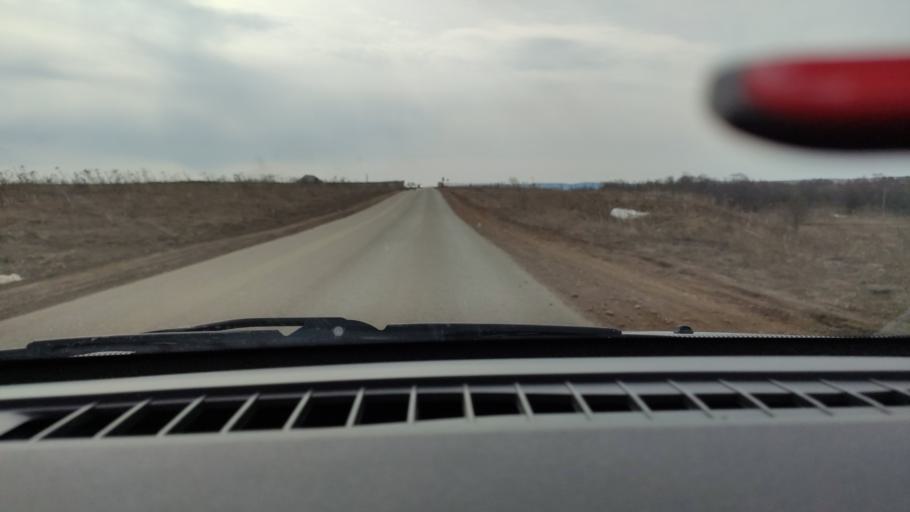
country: RU
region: Perm
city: Kultayevo
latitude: 57.9023
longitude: 55.9926
